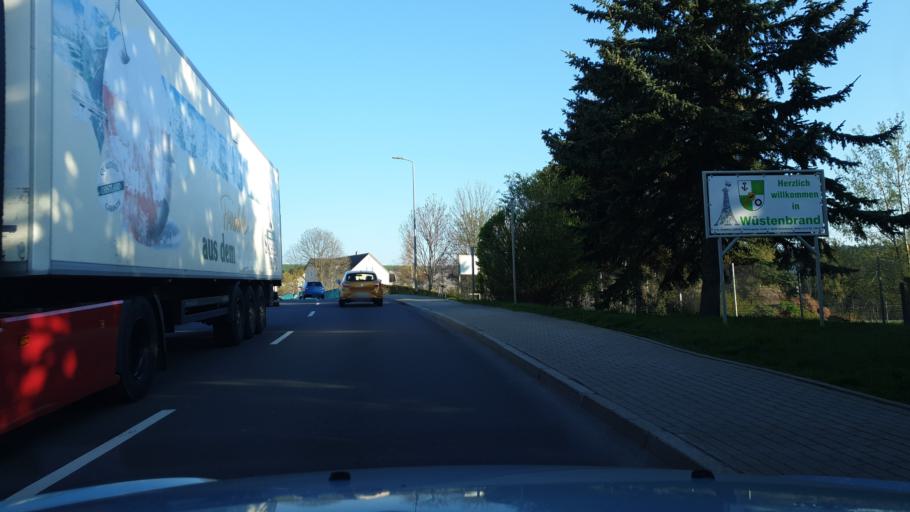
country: DE
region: Saxony
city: Kirchberg
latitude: 50.8054
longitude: 12.7599
